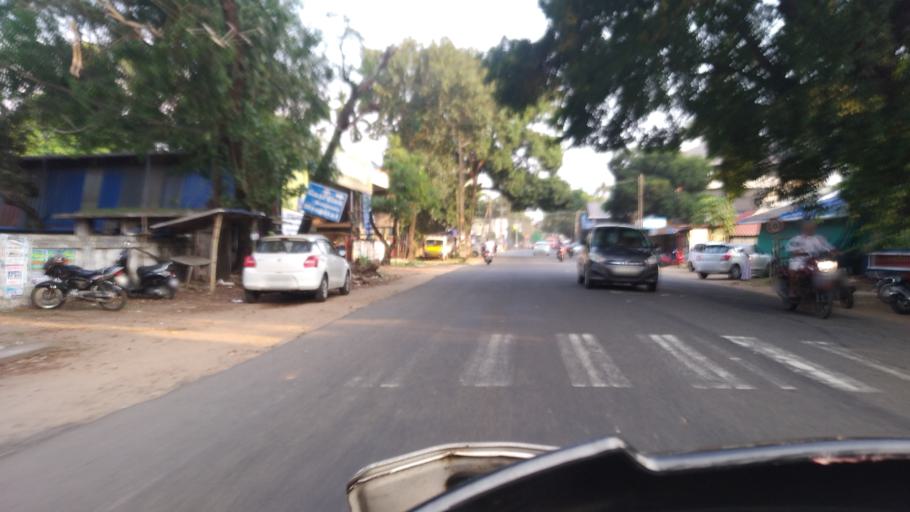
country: IN
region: Kerala
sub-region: Thrissur District
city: Irinjalakuda
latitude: 10.3253
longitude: 76.1436
